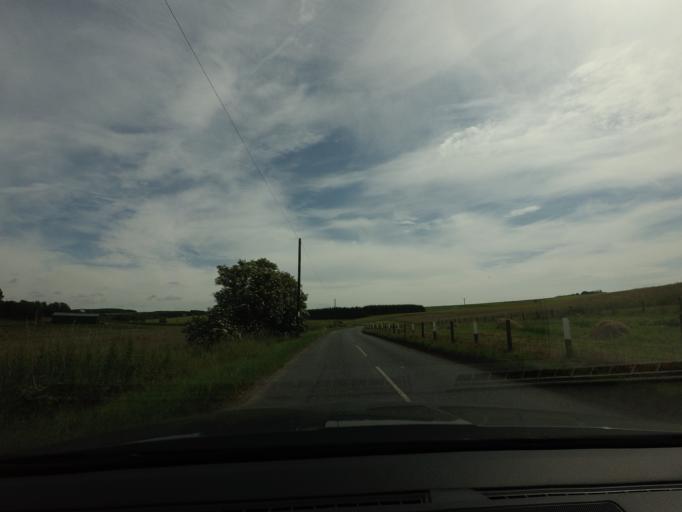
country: GB
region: Scotland
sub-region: Aberdeenshire
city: Turriff
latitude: 57.5706
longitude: -2.2987
